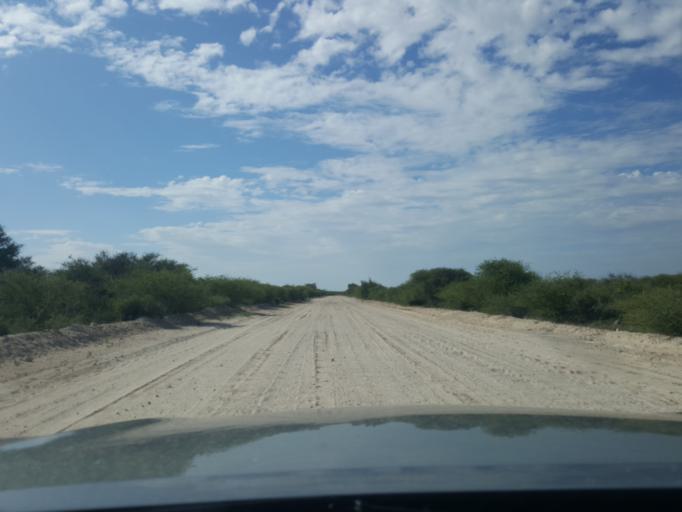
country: BW
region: Kweneng
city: Khudumelapye
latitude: -23.6002
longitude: 24.7229
